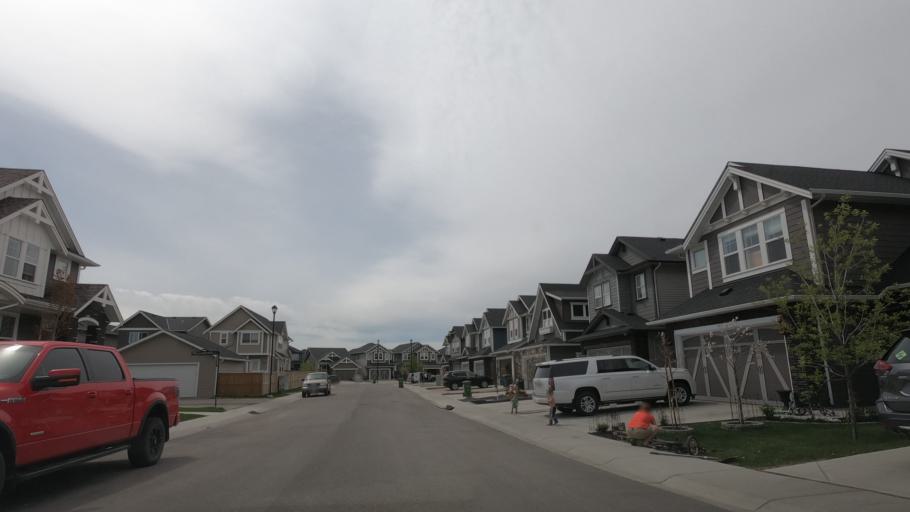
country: CA
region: Alberta
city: Airdrie
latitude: 51.3070
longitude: -114.0325
